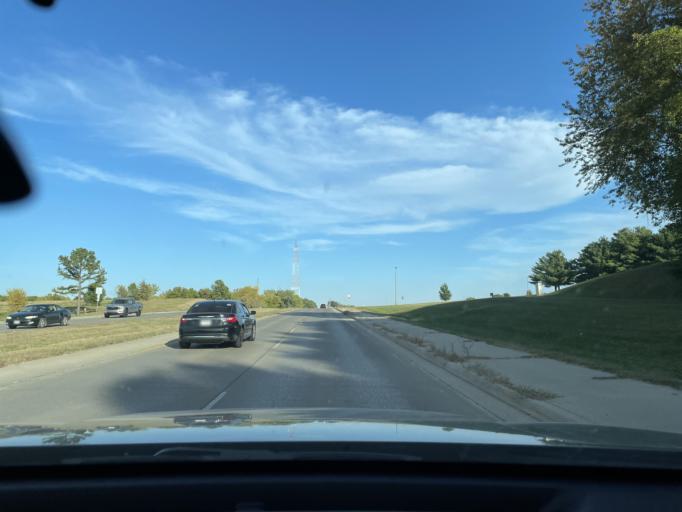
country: US
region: Missouri
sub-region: Buchanan County
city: Saint Joseph
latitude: 39.7696
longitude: -94.8115
